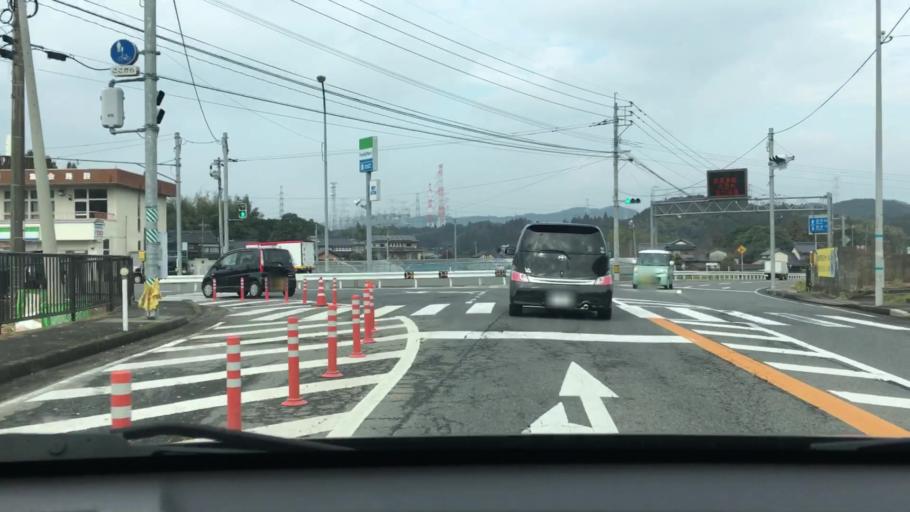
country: JP
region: Saga Prefecture
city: Imaricho-ko
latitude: 33.3379
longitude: 129.9313
